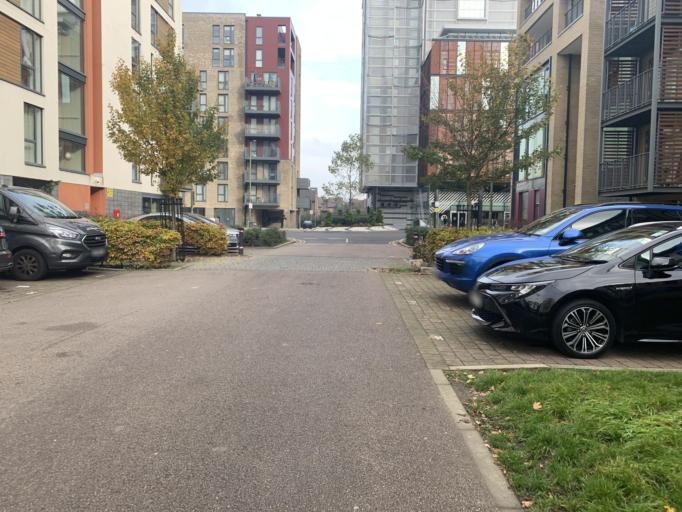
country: GB
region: England
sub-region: Greater London
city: Edgware
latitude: 51.5953
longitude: -0.2517
